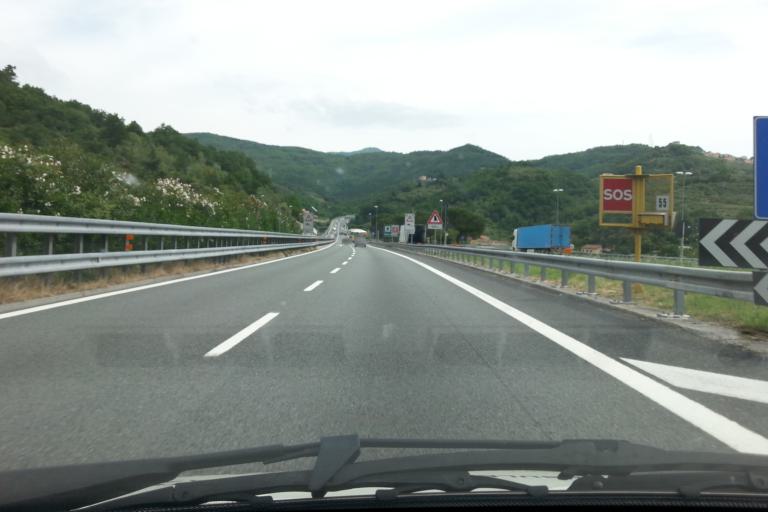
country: IT
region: Liguria
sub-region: Provincia di Savona
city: Feglino
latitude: 44.2122
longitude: 8.3209
